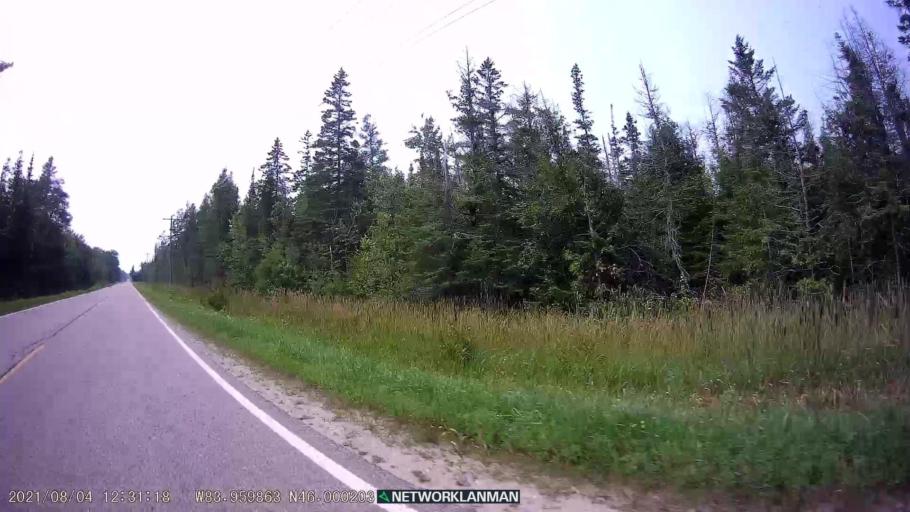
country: CA
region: Ontario
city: Thessalon
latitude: 46.0002
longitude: -83.9609
